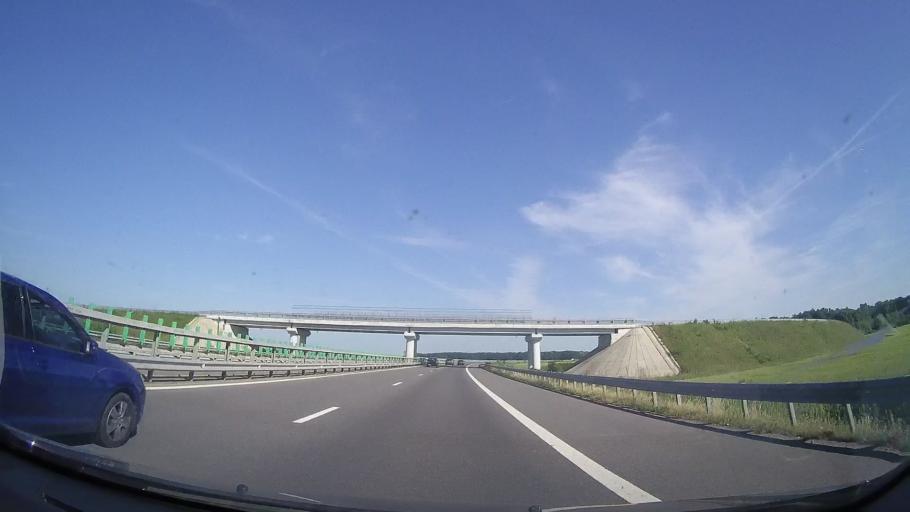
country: RO
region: Prahova
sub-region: Comuna Dumbrava
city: Dumbrava
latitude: 44.8578
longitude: 26.1970
